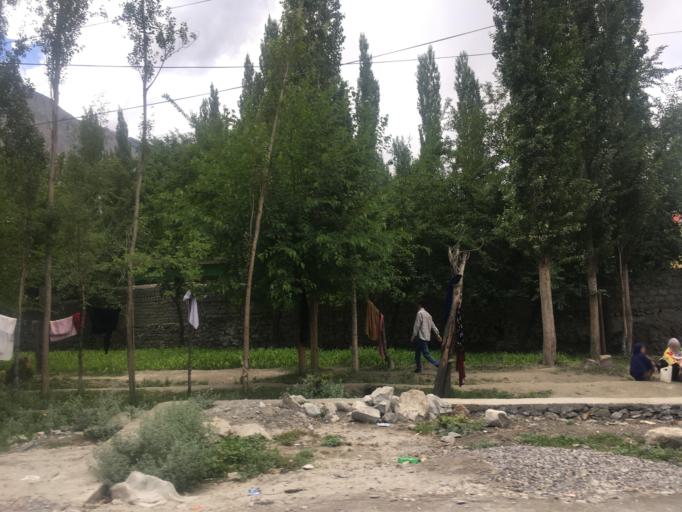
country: PK
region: Gilgit-Baltistan
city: Skardu
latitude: 35.2921
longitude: 75.6139
